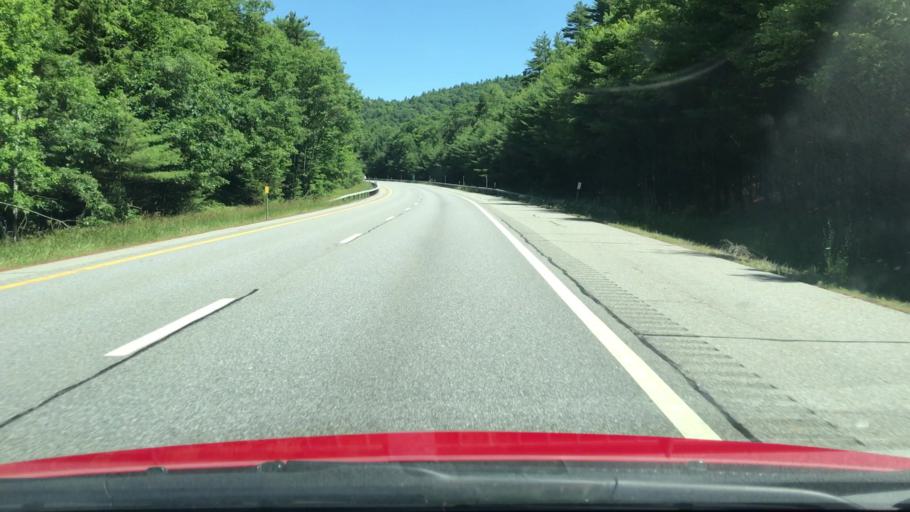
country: US
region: New York
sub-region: Warren County
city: Warrensburg
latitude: 43.5168
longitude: -73.7403
